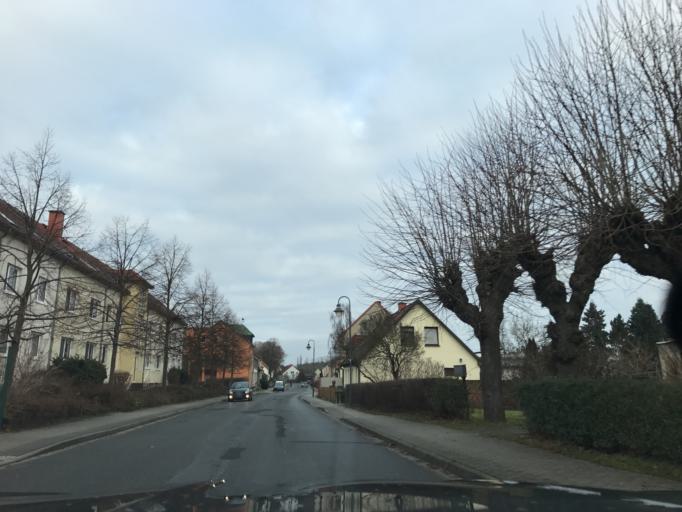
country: DE
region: Brandenburg
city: Gross Kreutz
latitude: 52.3199
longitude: 12.7367
